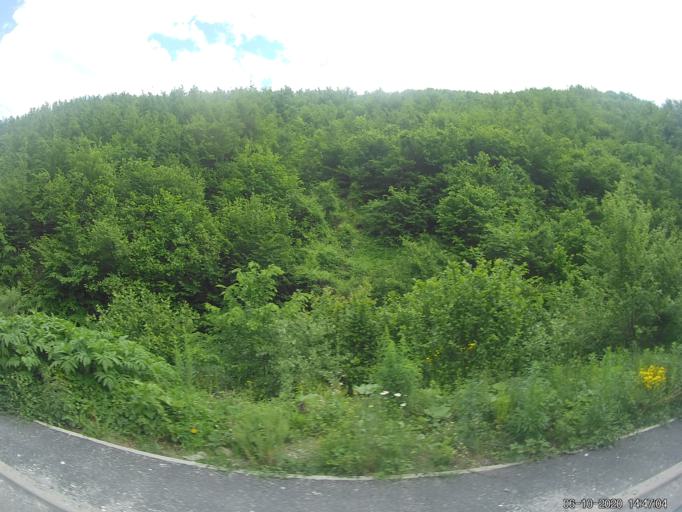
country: XK
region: Prizren
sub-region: Komuna e Therandes
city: Budakovo
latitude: 42.3858
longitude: 20.9592
